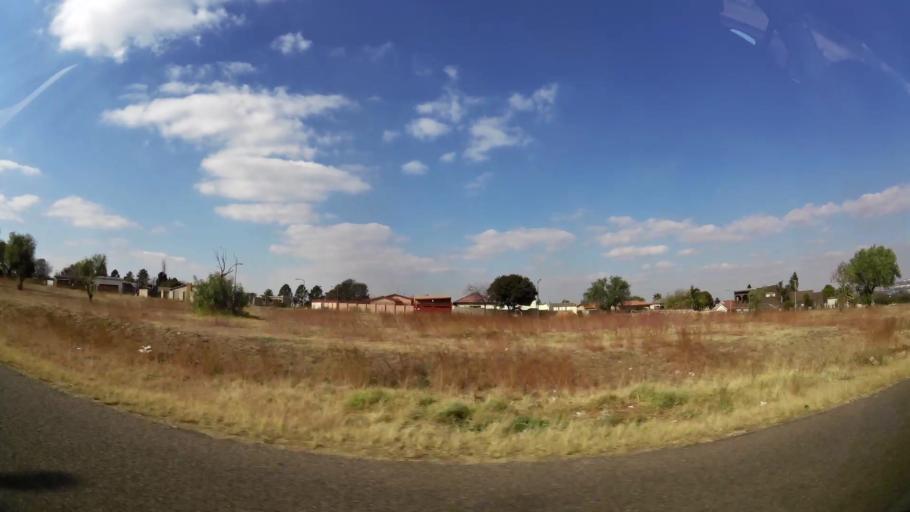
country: ZA
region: Gauteng
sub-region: West Rand District Municipality
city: Krugersdorp
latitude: -26.0751
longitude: 27.7610
